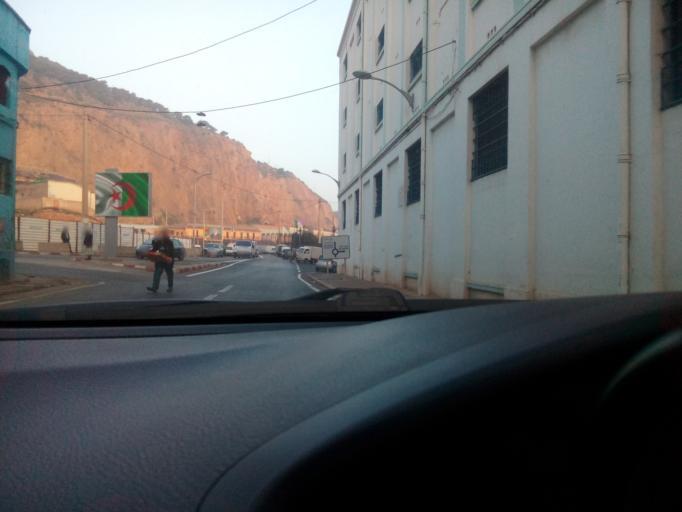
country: DZ
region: Oran
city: Oran
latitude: 35.7082
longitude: -0.6551
